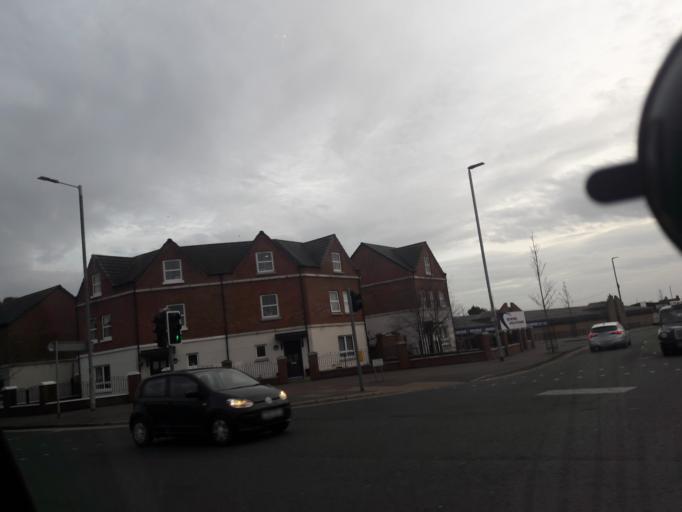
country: GB
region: Northern Ireland
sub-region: City of Belfast
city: Belfast
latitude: 54.6095
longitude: -5.9458
